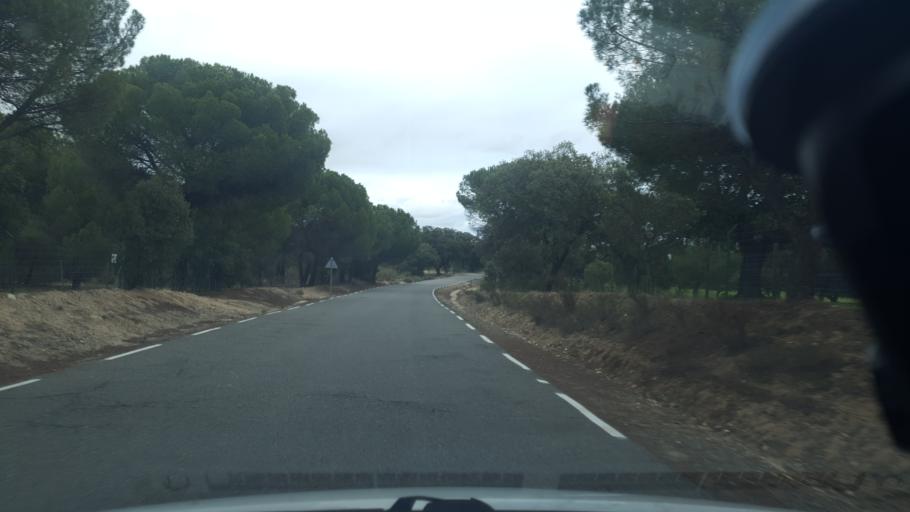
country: ES
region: Castille and Leon
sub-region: Provincia de Avila
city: Pozanco
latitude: 40.8268
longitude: -4.6989
